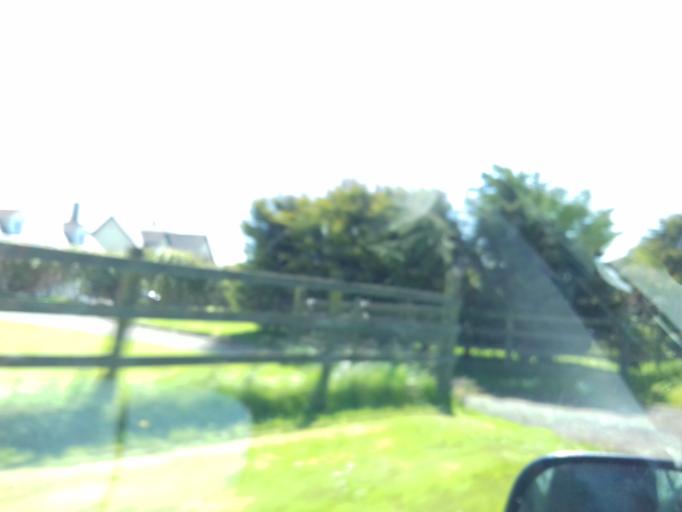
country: IE
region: Munster
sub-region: Waterford
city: Dunmore East
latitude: 52.1928
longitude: -6.8554
